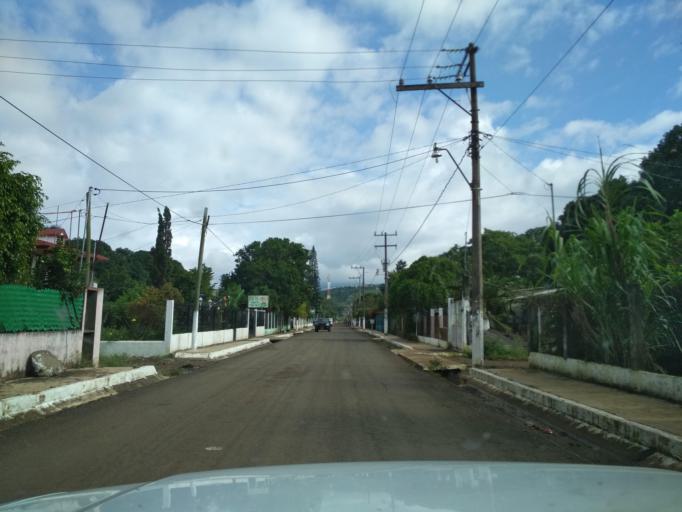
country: MX
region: Veracruz
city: Catemaco
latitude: 18.3768
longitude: -95.1252
